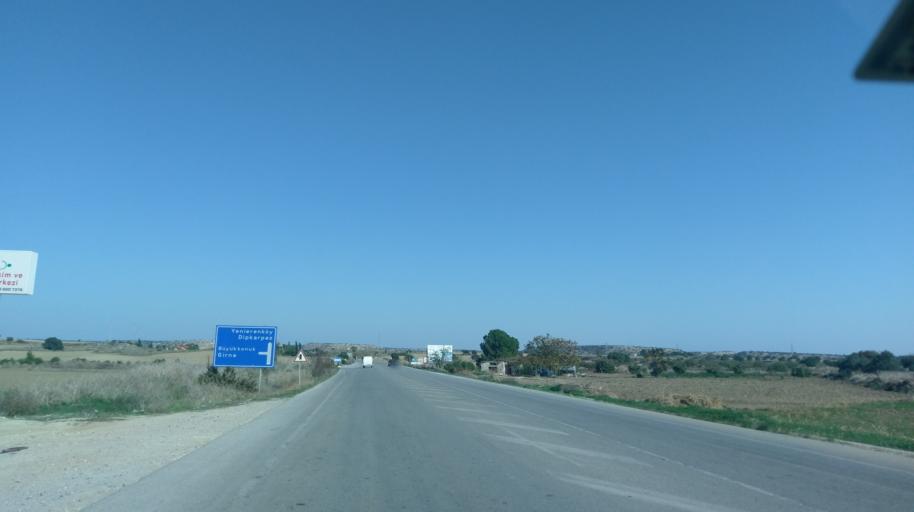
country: CY
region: Ammochostos
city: Leonarisso
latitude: 35.3708
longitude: 34.0322
